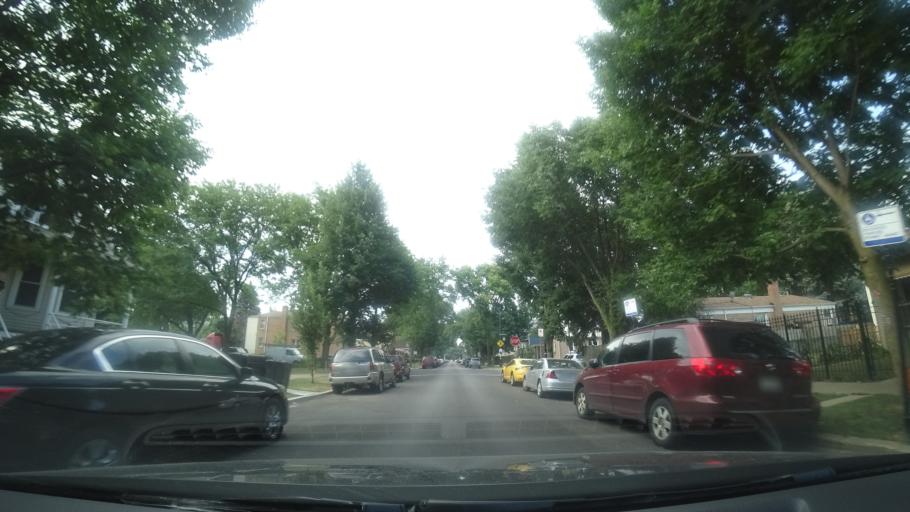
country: US
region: Illinois
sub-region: Cook County
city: Lincolnwood
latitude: 41.9413
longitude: -87.7371
